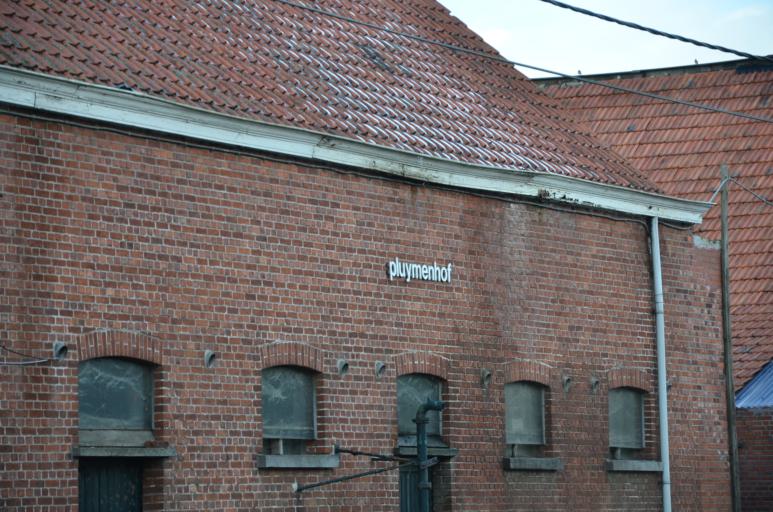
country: BE
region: Flanders
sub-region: Provincie Antwerpen
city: Lille
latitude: 51.2375
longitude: 4.8057
